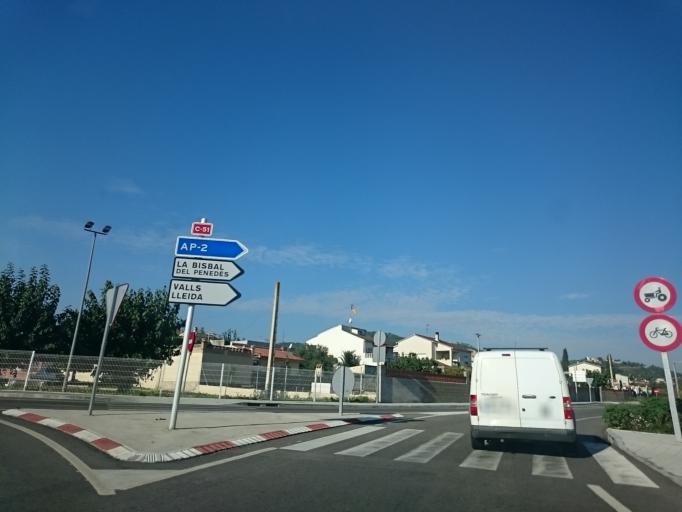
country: ES
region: Catalonia
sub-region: Provincia de Tarragona
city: Albinyana
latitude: 41.2555
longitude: 1.5048
